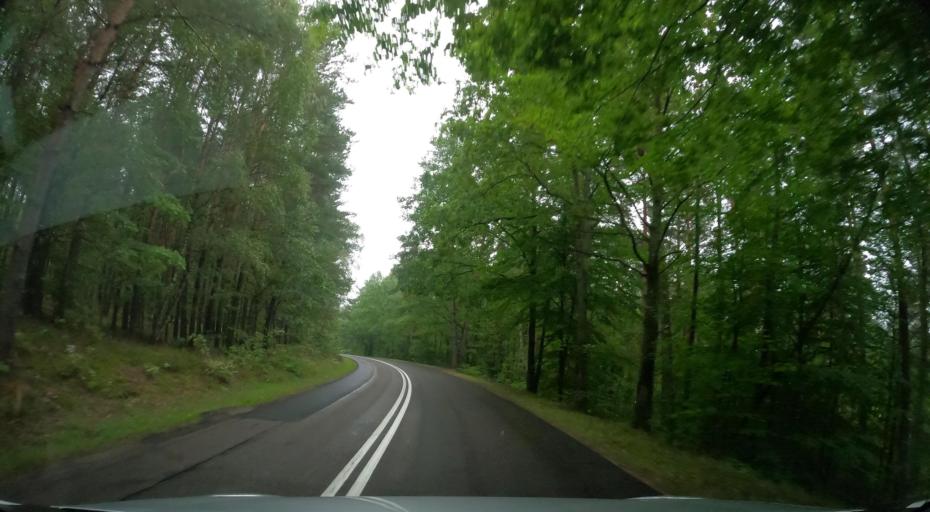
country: PL
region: Pomeranian Voivodeship
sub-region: Powiat wejherowski
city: Linia
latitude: 54.4624
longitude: 17.9963
